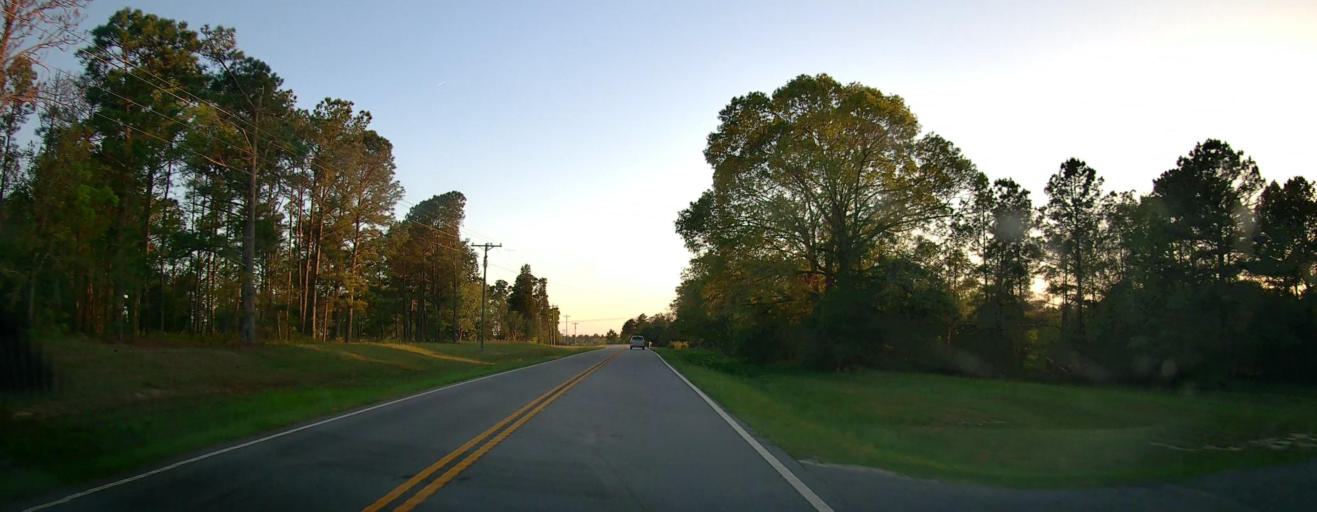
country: US
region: Georgia
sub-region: Talbot County
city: Talbotton
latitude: 32.5045
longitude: -84.6090
